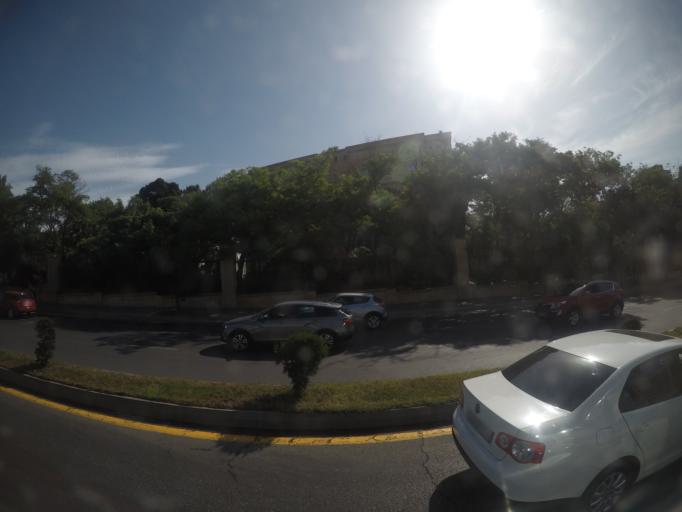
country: AZ
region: Baki
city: Badamdar
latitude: 40.3881
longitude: 49.8269
